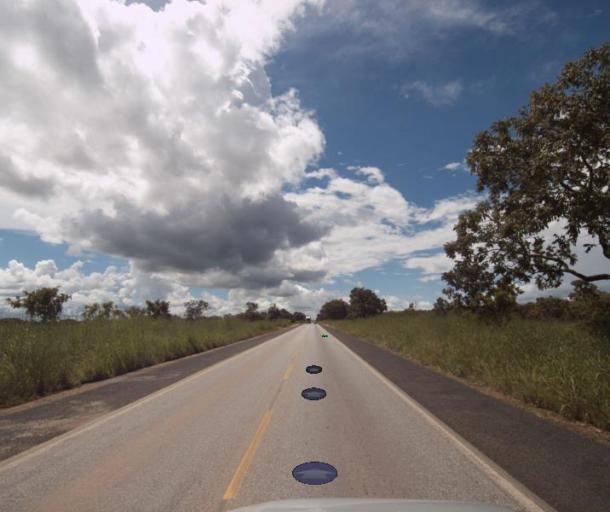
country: BR
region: Goias
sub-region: Uruacu
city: Uruacu
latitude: -14.0203
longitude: -49.0869
